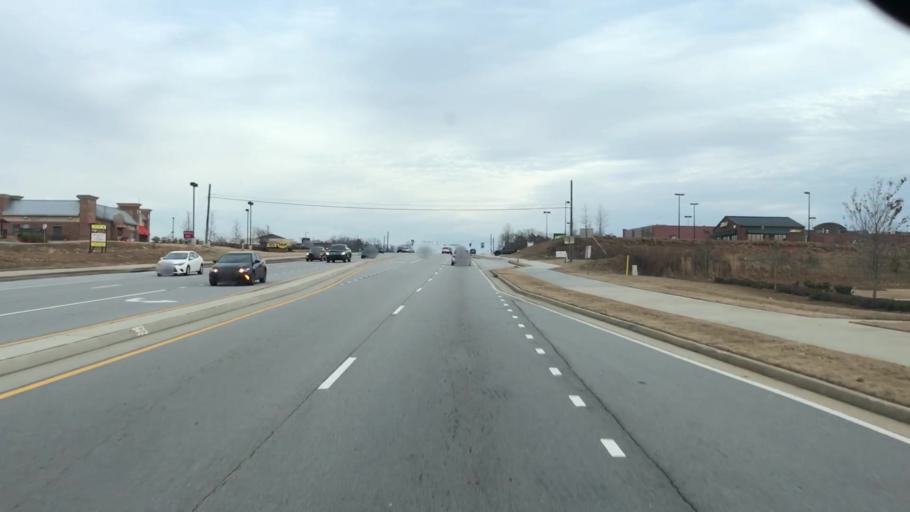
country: US
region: Georgia
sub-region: Hall County
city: Flowery Branch
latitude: 34.1090
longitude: -83.8783
